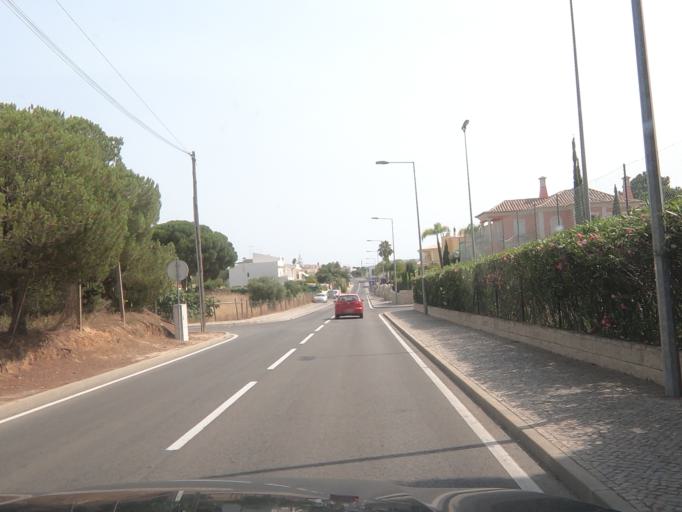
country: PT
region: Faro
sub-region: Loule
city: Quarteira
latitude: 37.0784
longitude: -8.0782
